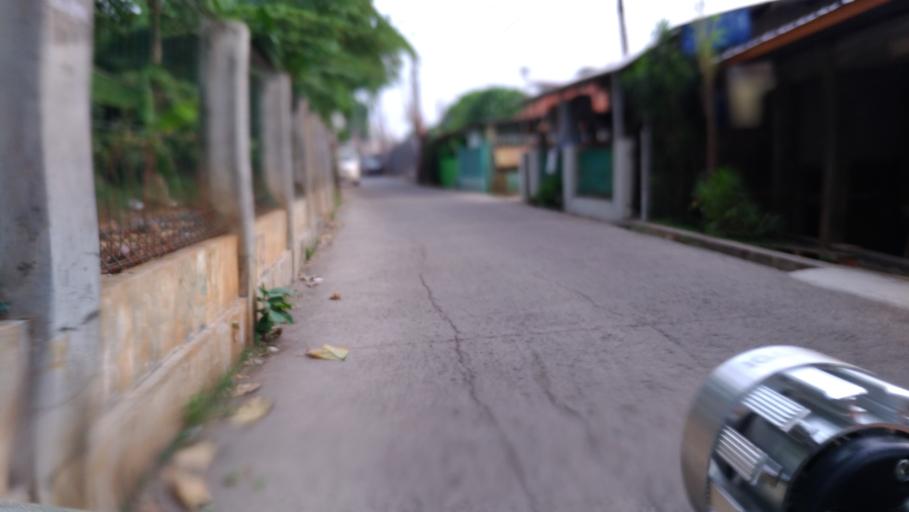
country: ID
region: West Java
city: Depok
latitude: -6.3600
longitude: 106.8664
